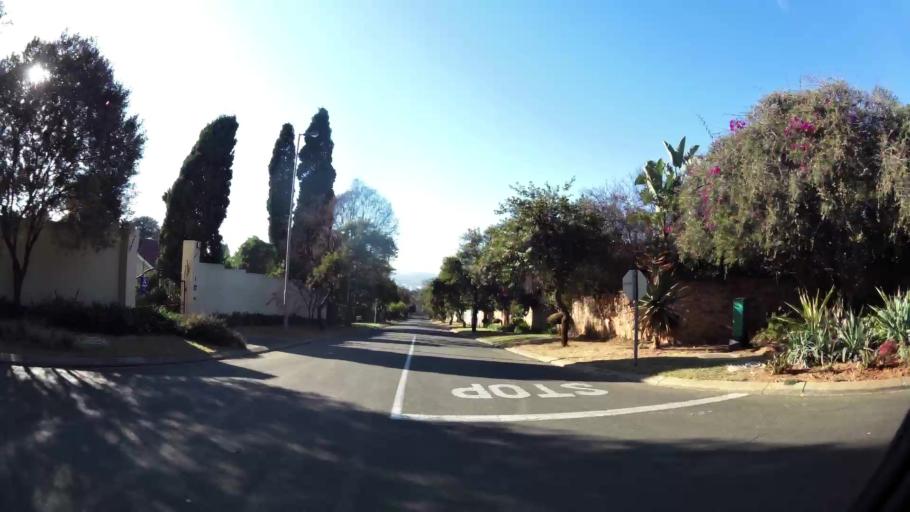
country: ZA
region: Gauteng
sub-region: City of Johannesburg Metropolitan Municipality
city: Midrand
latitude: -26.0291
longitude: 28.0442
